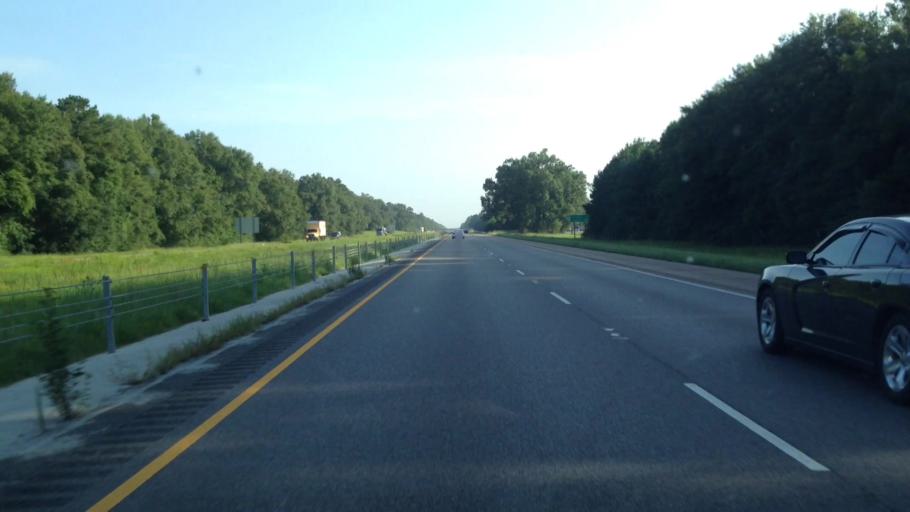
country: US
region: Louisiana
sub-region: Tangipahoa Parish
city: Natalbany
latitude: 30.5314
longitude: -90.5038
